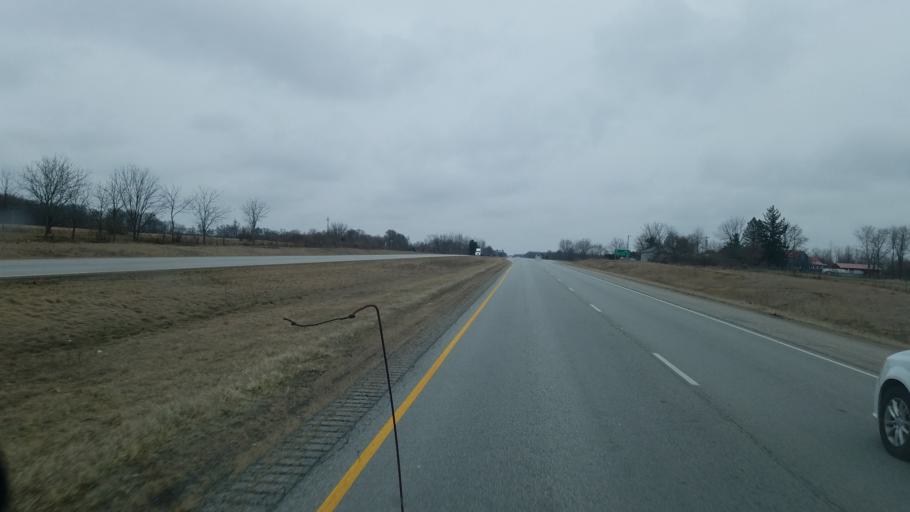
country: US
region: Indiana
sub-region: Fulton County
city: Rochester
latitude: 40.9633
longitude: -86.1685
